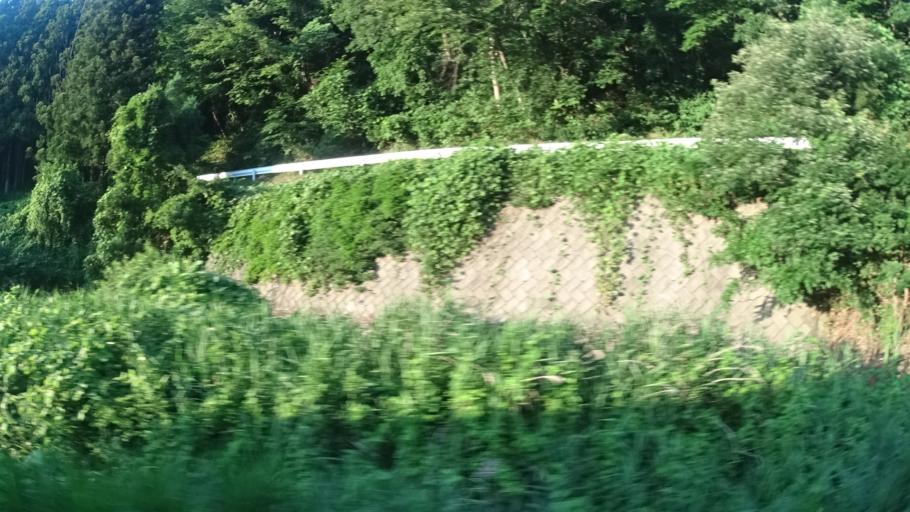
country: JP
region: Fukushima
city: Miharu
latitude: 37.4564
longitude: 140.5134
